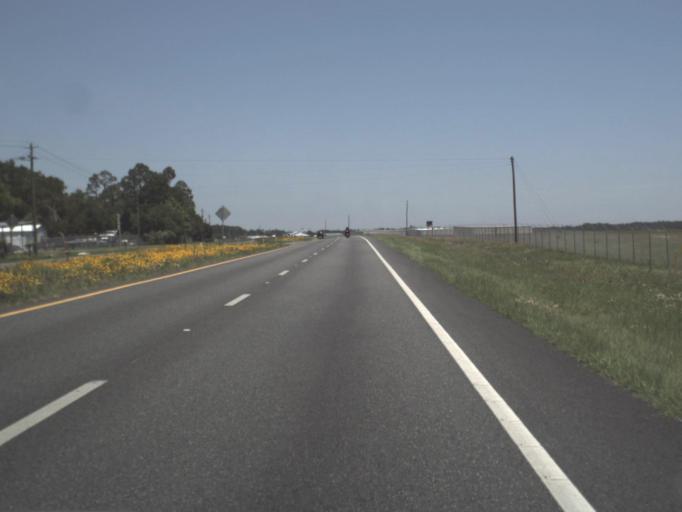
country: US
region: Florida
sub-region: Columbia County
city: Watertown
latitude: 30.1864
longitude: -82.5908
